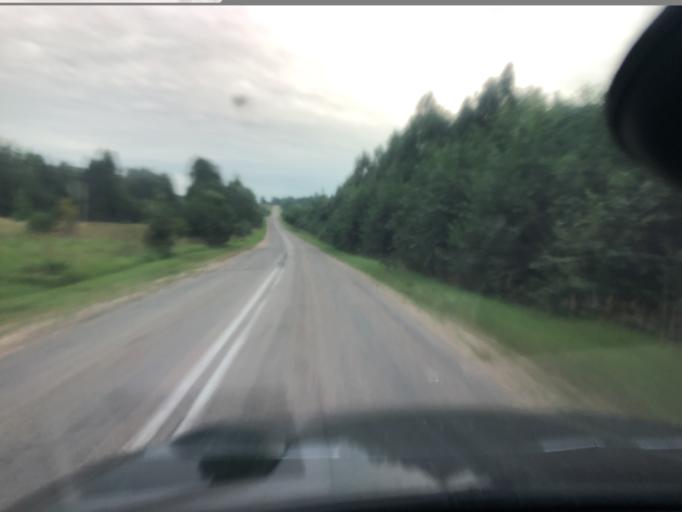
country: RU
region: Jaroslavl
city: Petrovsk
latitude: 56.9958
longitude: 39.1048
